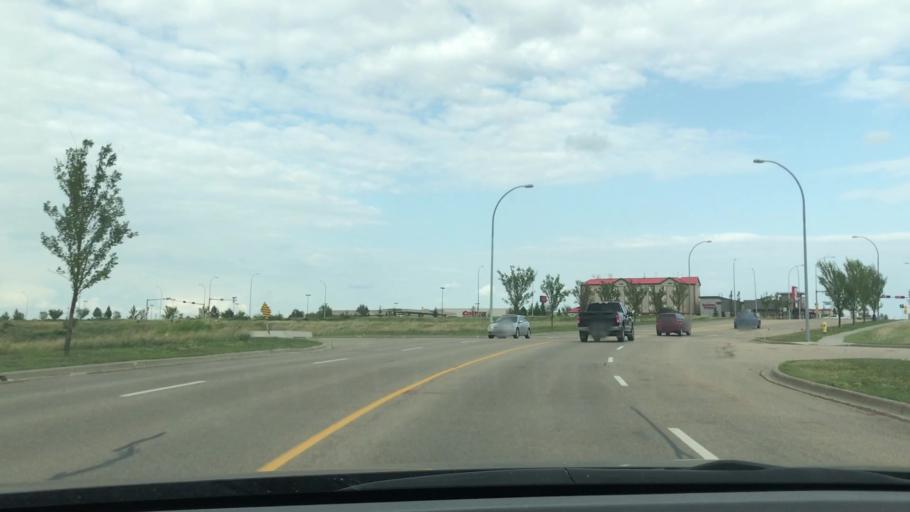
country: CA
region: Alberta
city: Sherwood Park
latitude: 53.5450
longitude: -113.3235
